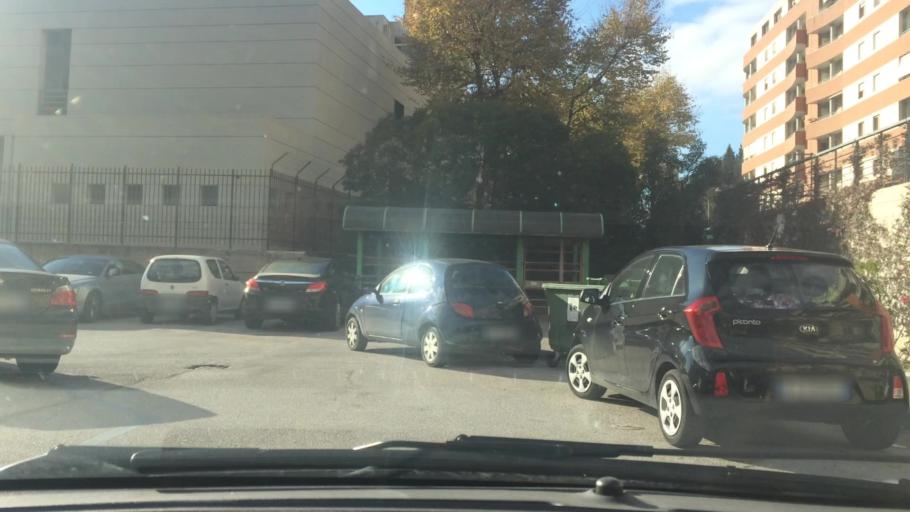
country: IT
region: Basilicate
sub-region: Provincia di Matera
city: Matera
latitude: 40.6668
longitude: 16.5999
